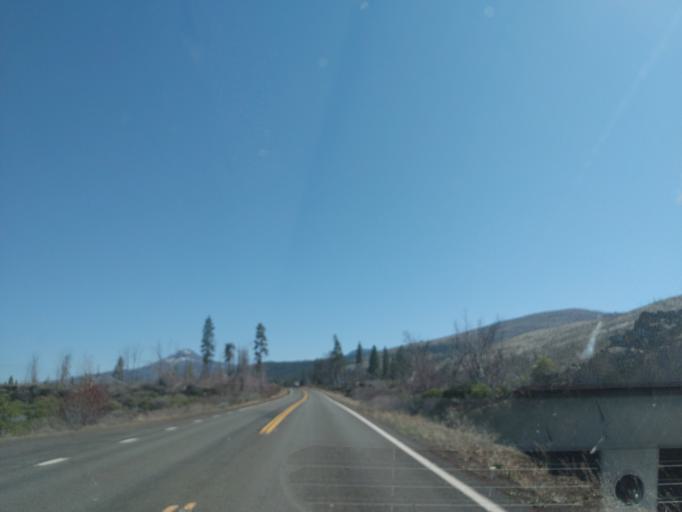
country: US
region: California
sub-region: Shasta County
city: Burney
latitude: 40.7763
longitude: -121.5030
